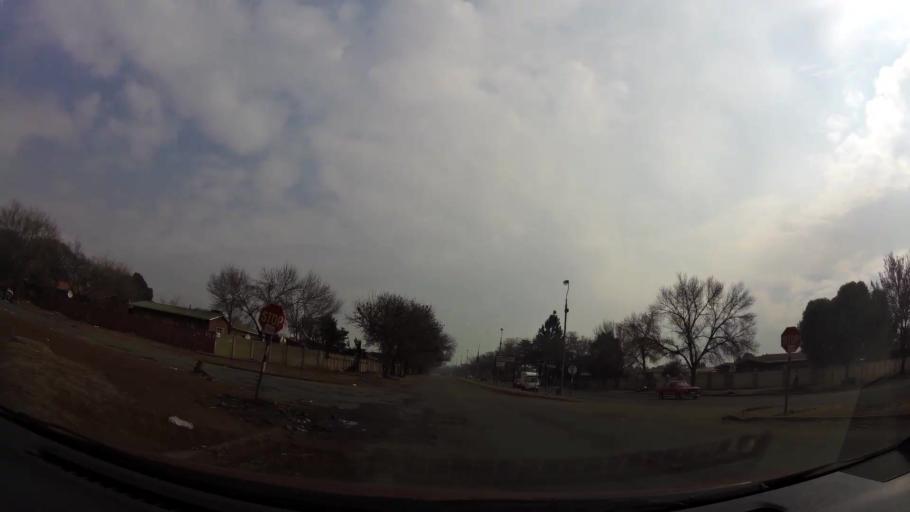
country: ZA
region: Gauteng
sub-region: Sedibeng District Municipality
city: Vanderbijlpark
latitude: -26.6873
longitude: 27.8433
